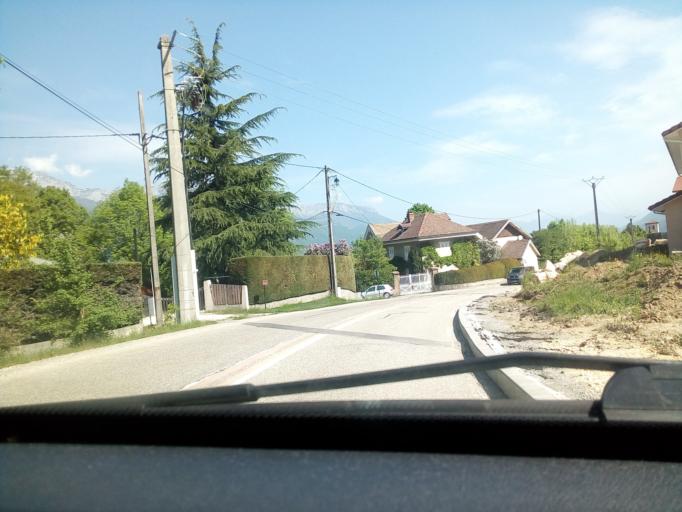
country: FR
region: Rhone-Alpes
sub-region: Departement de l'Isere
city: Le Champ-pres-Froges
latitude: 45.2767
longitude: 5.9383
